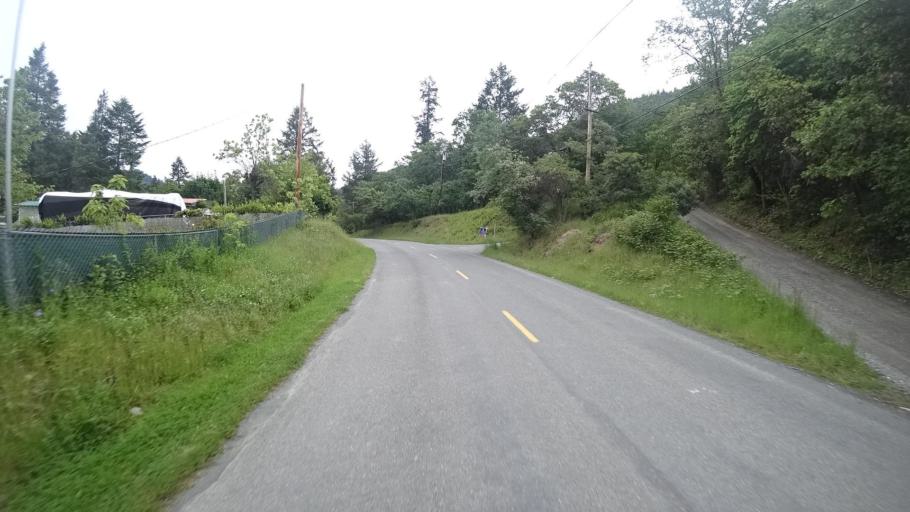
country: US
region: California
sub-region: Humboldt County
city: Willow Creek
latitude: 40.9692
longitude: -123.6306
